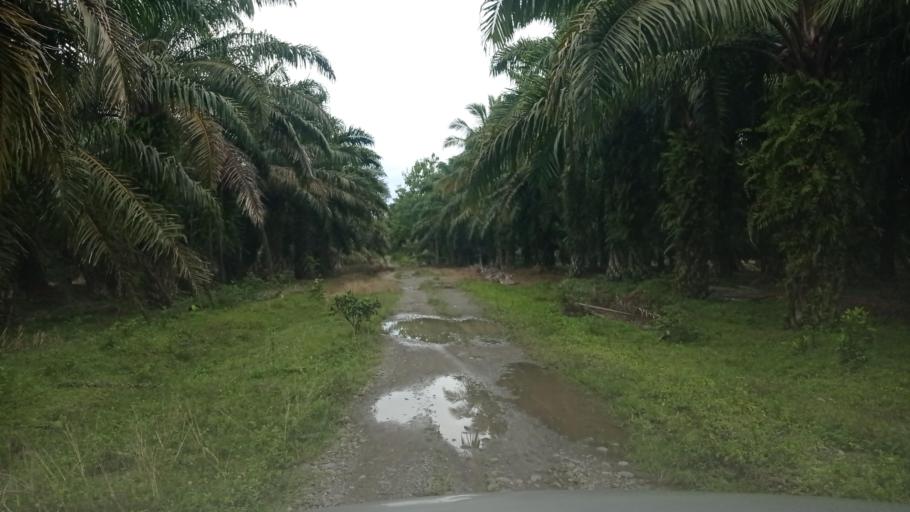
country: ID
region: Jambi
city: Sungai Penuh
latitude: -2.5148
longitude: 101.0733
